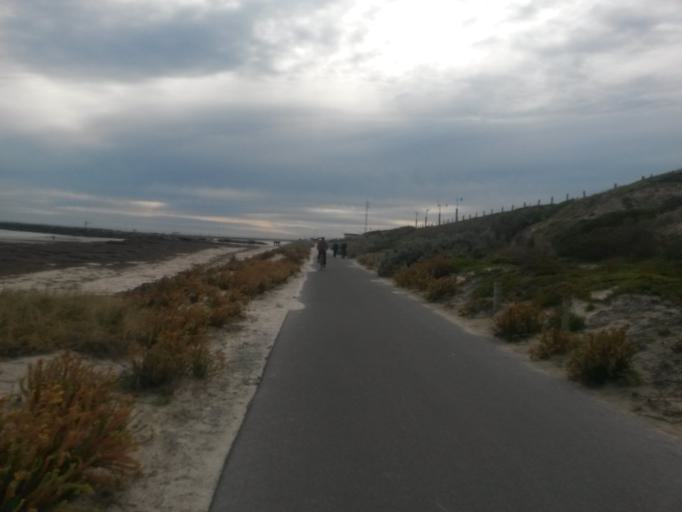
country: AU
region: South Australia
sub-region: Adelaide
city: Glenelg
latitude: -34.9611
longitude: 138.5072
